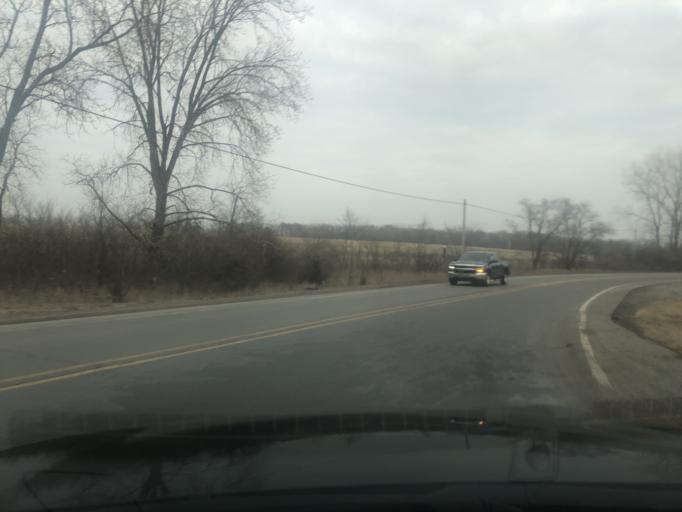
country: US
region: Michigan
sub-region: Wayne County
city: Belleville
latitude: 42.2207
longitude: -83.5471
